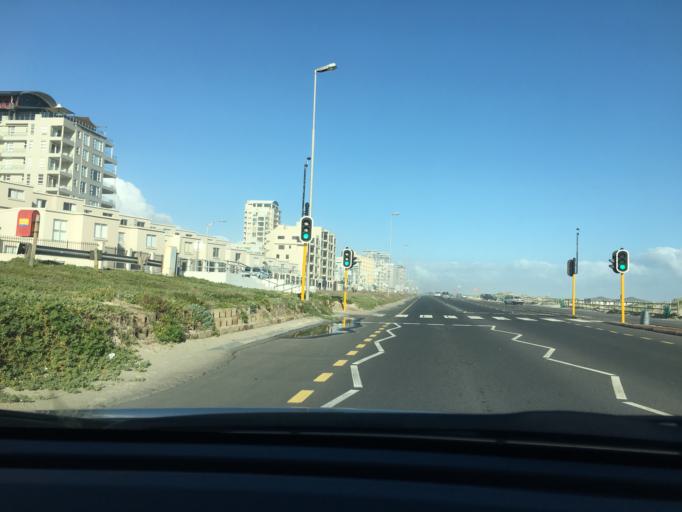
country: ZA
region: Western Cape
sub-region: City of Cape Town
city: Sunset Beach
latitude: -33.8152
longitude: 18.4723
